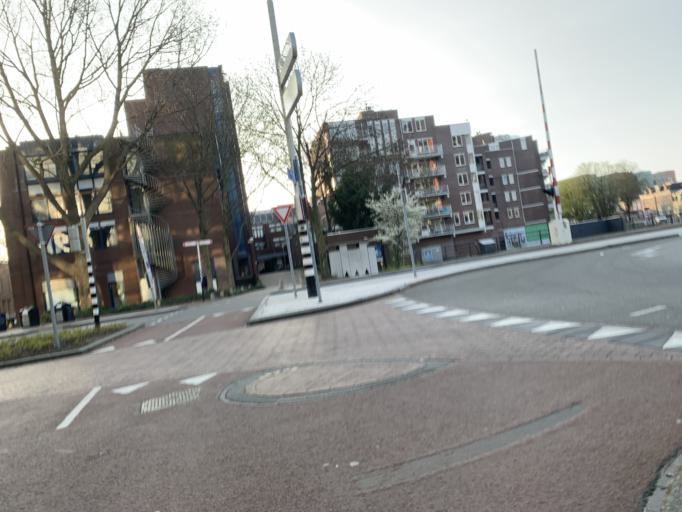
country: NL
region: Groningen
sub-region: Gemeente Groningen
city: Groningen
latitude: 53.2143
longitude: 6.5557
